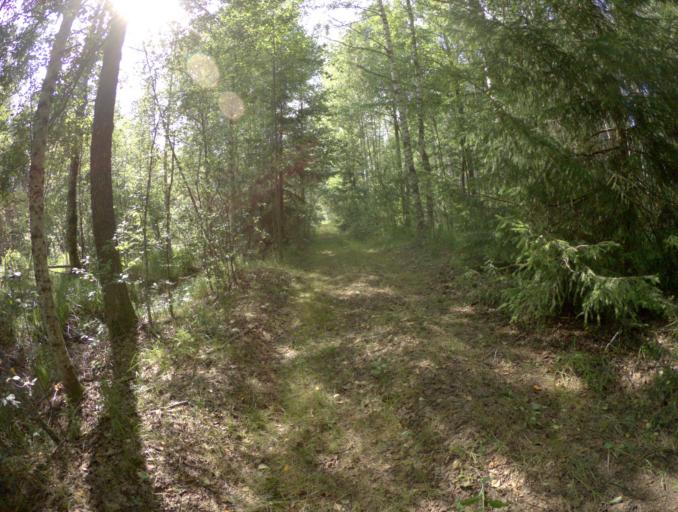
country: RU
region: Vladimir
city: Vorsha
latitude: 55.8989
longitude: 40.1638
